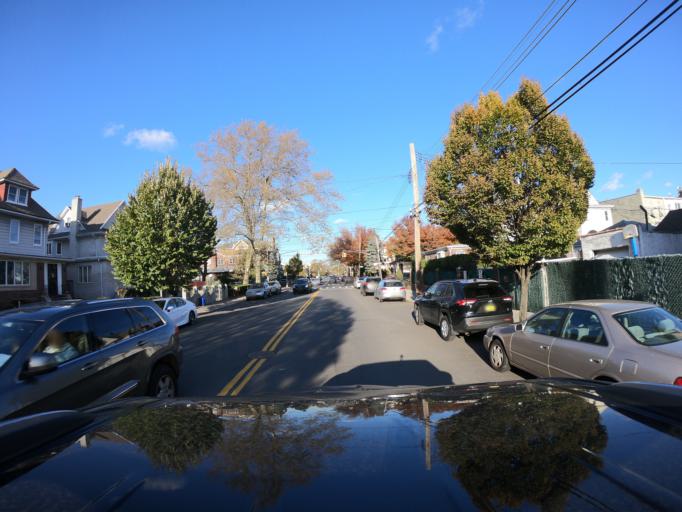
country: US
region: New York
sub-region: Kings County
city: Bensonhurst
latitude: 40.6198
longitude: -74.0040
